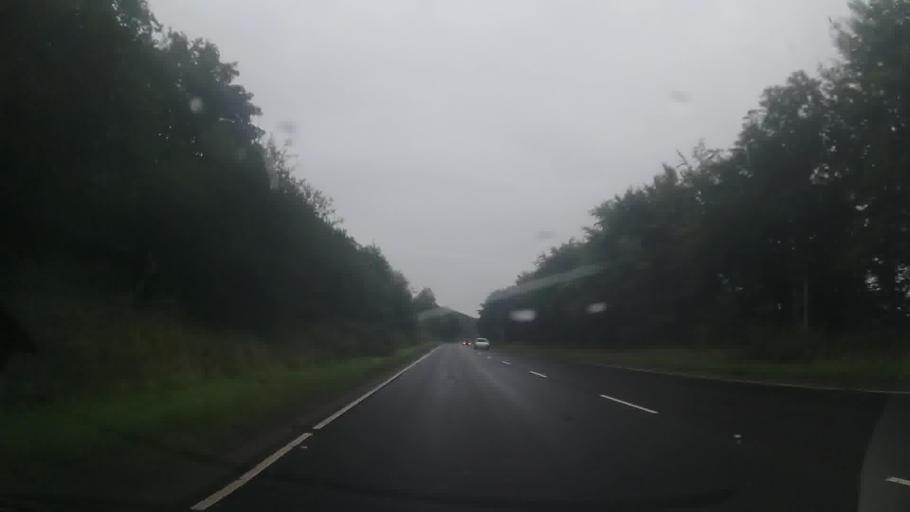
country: GB
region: Scotland
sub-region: North Ayrshire
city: Fairlie
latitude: 55.7265
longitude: -4.8647
